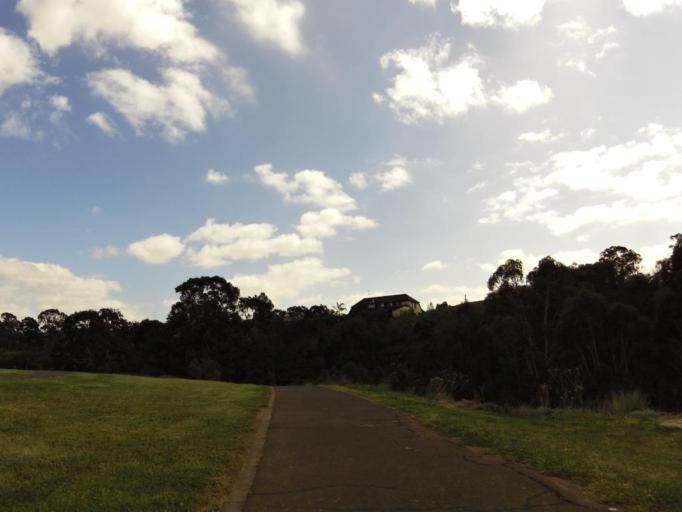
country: AU
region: Victoria
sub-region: Brimbank
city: Kealba
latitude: -37.7295
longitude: 144.8412
